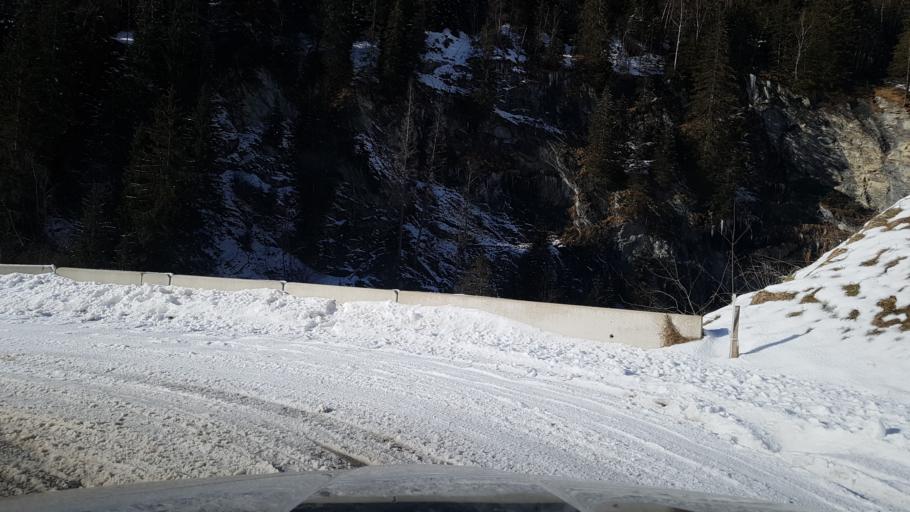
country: AT
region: Salzburg
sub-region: Politischer Bezirk Sankt Johann im Pongau
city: Huttschlag
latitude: 47.1707
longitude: 13.2641
